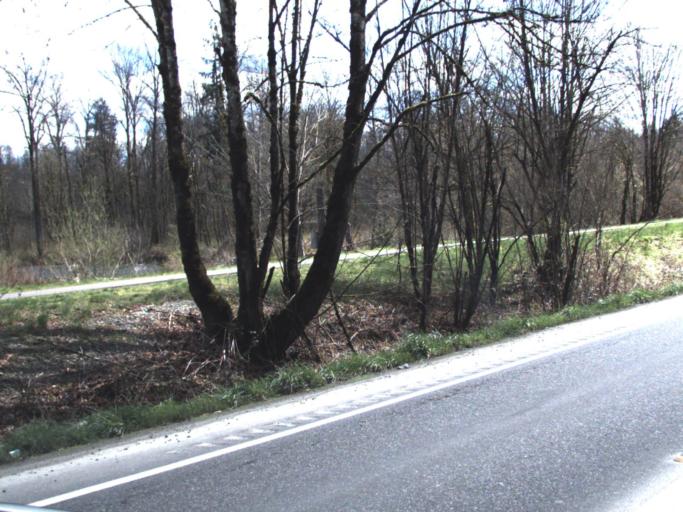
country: US
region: Washington
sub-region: King County
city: Maple Heights-Lake Desire
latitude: 47.4488
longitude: -122.0739
